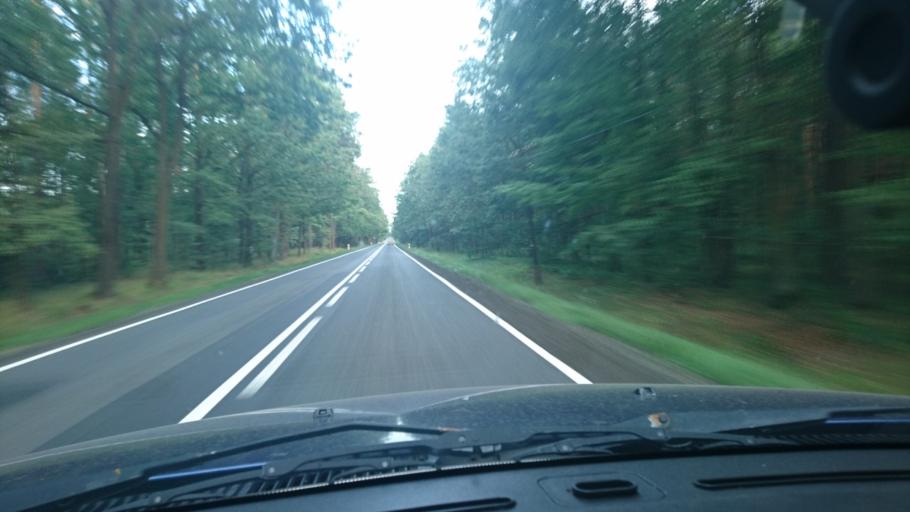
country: PL
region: Opole Voivodeship
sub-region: Powiat oleski
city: Olesno
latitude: 50.8500
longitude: 18.4705
